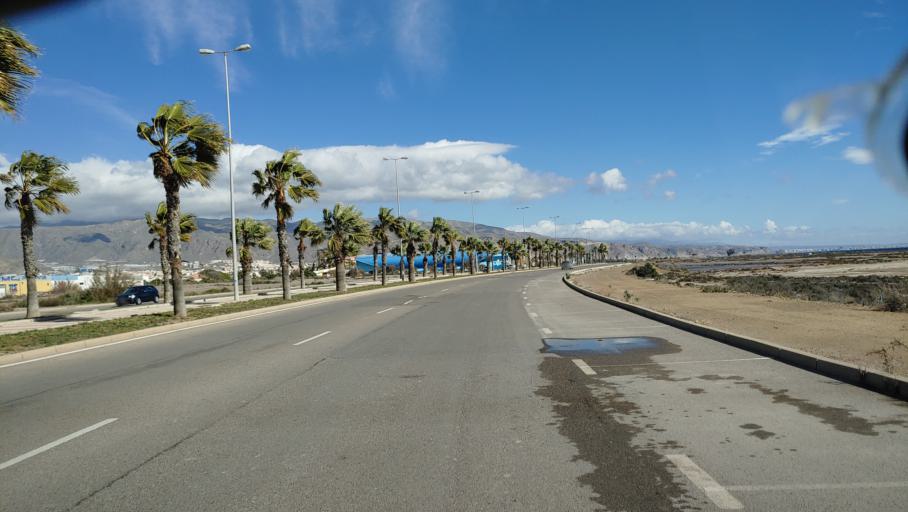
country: ES
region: Andalusia
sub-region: Provincia de Almeria
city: Roquetas de Mar
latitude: 36.7793
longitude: -2.6062
